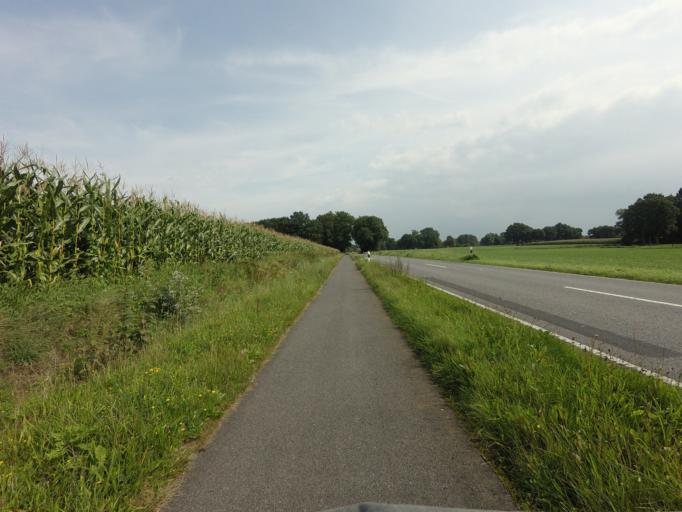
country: DE
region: Lower Saxony
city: Lage
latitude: 52.4744
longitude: 6.9422
